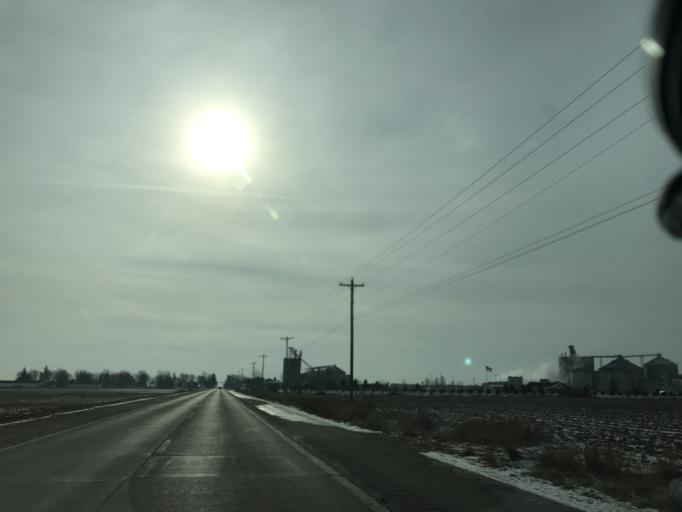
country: US
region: Michigan
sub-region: Ionia County
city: Lake Odessa
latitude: 42.7688
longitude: -85.0743
